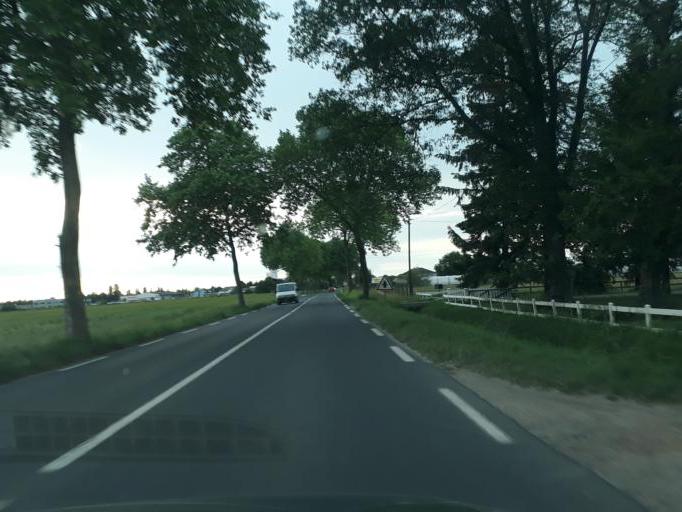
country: FR
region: Centre
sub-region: Departement du Loiret
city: Saint-Denis-en-Val
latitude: 47.8707
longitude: 1.9518
